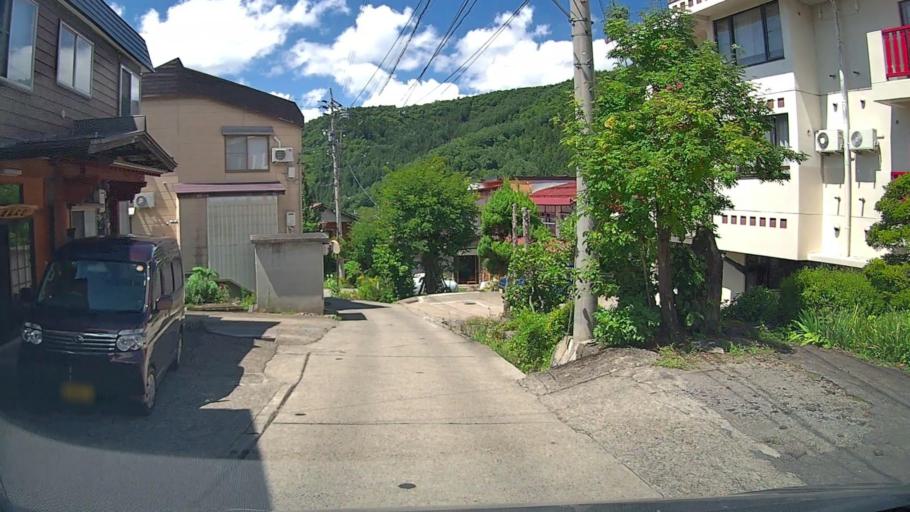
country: JP
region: Nagano
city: Iiyama
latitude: 36.9208
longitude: 138.4490
